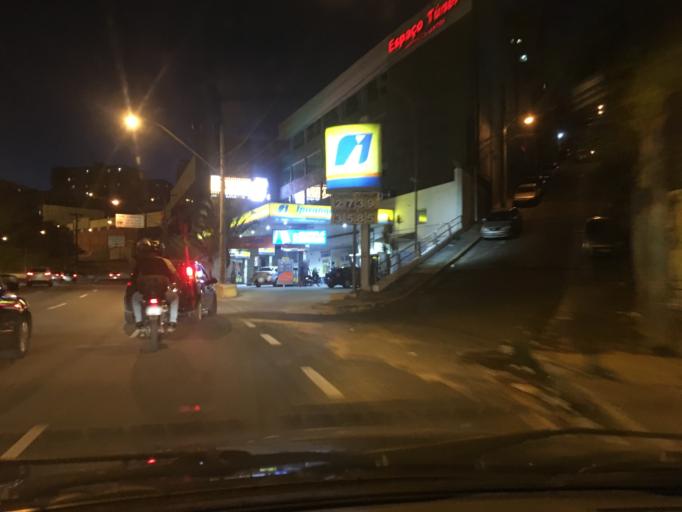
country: BR
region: Minas Gerais
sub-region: Belo Horizonte
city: Belo Horizonte
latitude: -19.9050
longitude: -43.9365
